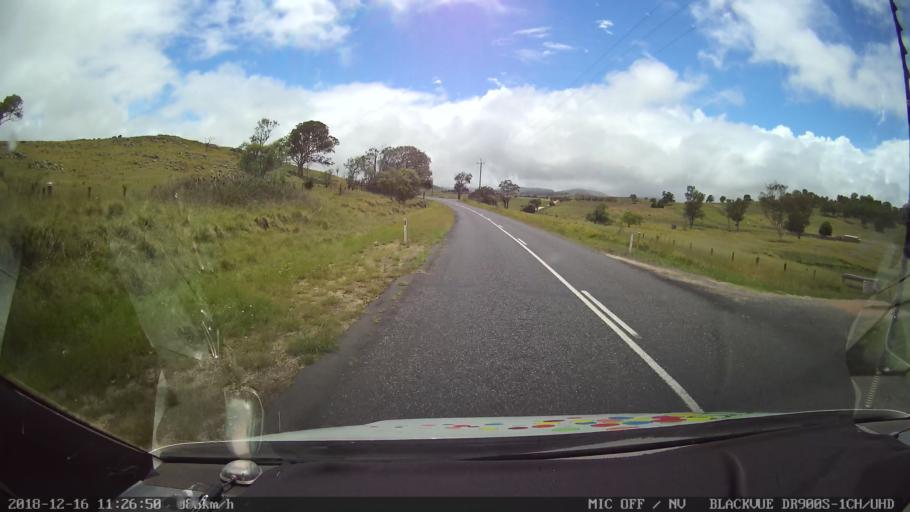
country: AU
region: New South Wales
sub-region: Tenterfield Municipality
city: Carrolls Creek
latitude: -29.0497
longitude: 152.0795
